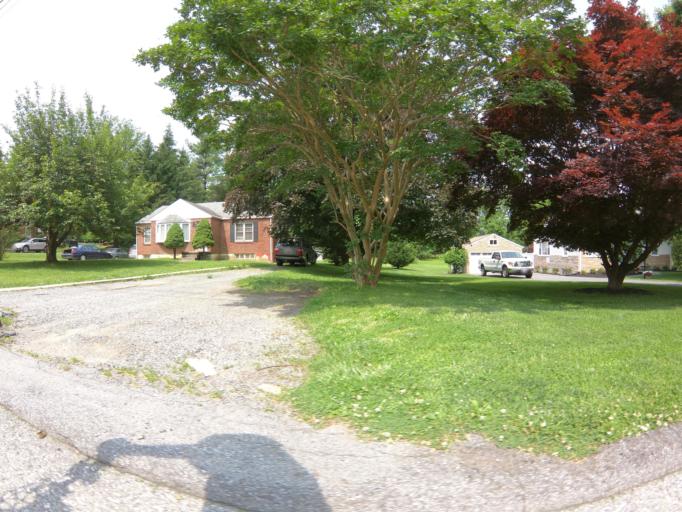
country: US
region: Maryland
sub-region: Howard County
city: Columbia
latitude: 39.2354
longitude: -76.8080
